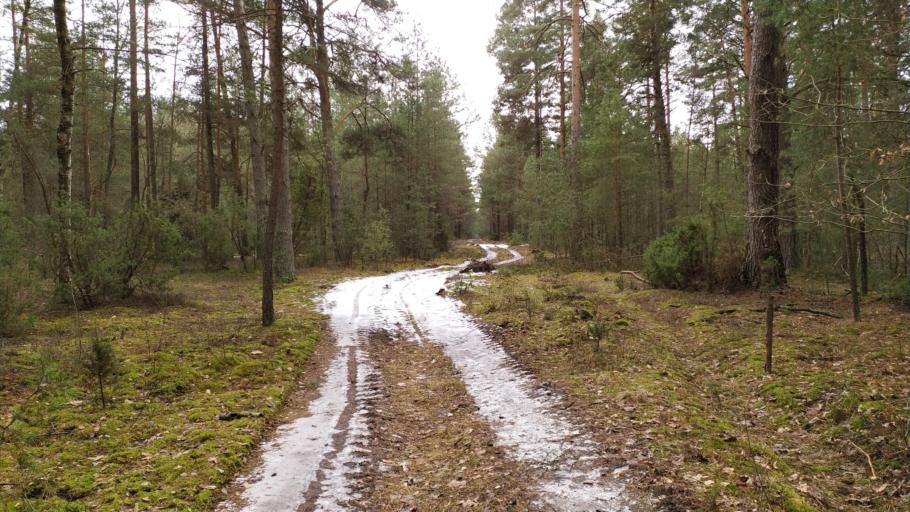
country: BY
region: Brest
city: Kamyanyets
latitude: 52.4354
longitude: 23.9998
